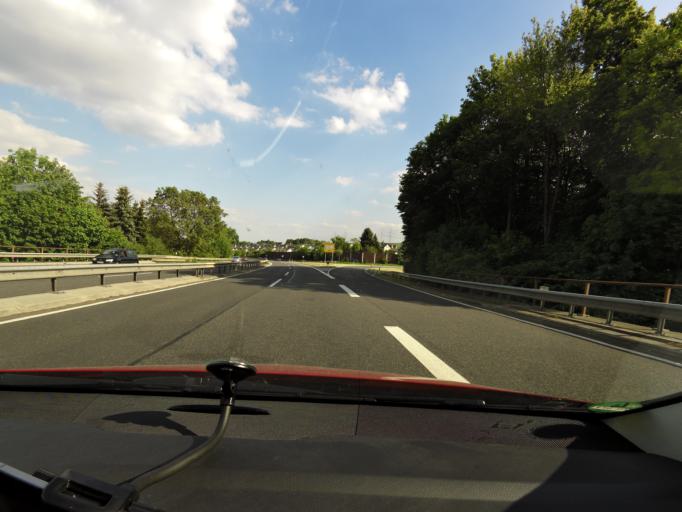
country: DE
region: Rheinland-Pfalz
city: Andernach
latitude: 50.4258
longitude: 7.3891
